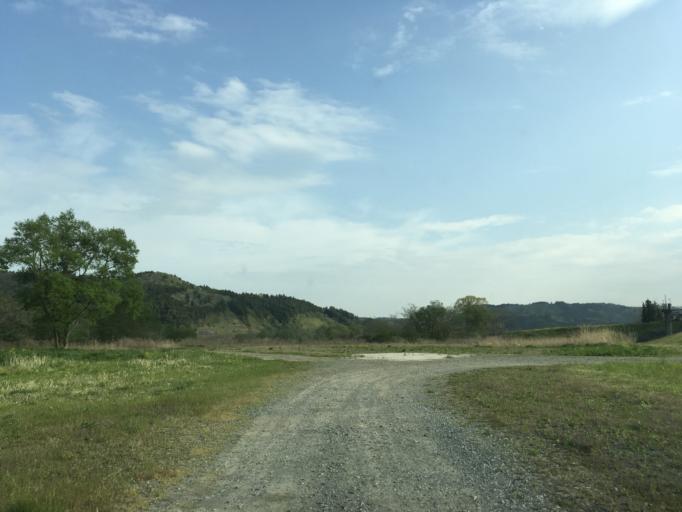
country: JP
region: Iwate
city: Ichinoseki
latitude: 38.8945
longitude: 141.2625
